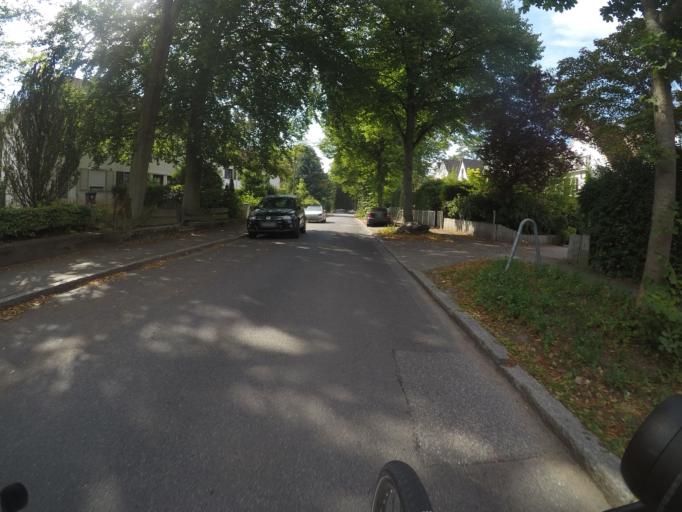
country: DE
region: Hamburg
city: Marienthal
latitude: 53.5670
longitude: 10.0852
